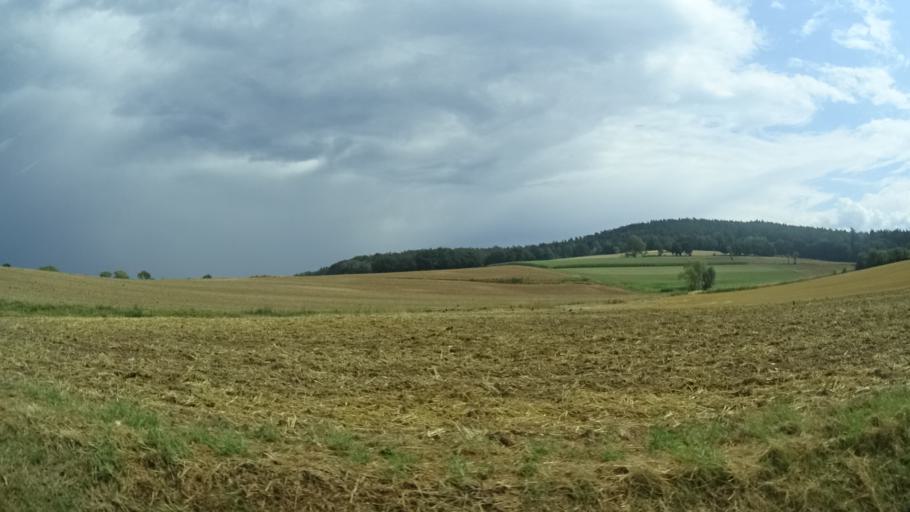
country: DE
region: Hesse
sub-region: Regierungsbezirk Kassel
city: Niederaula
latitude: 50.8055
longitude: 9.6399
